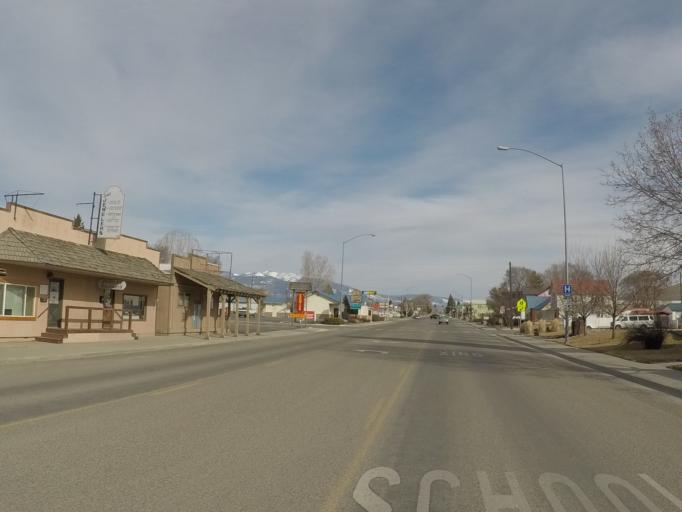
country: US
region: Idaho
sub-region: Lemhi County
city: Salmon
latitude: 45.1745
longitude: -113.8911
